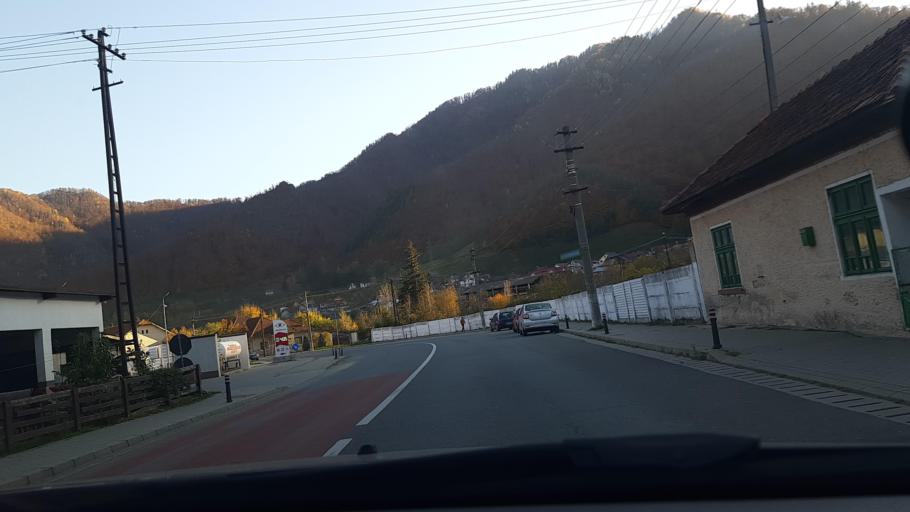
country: RO
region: Valcea
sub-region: Comuna Brezoi
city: Brezoi
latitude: 45.3389
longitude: 24.2474
